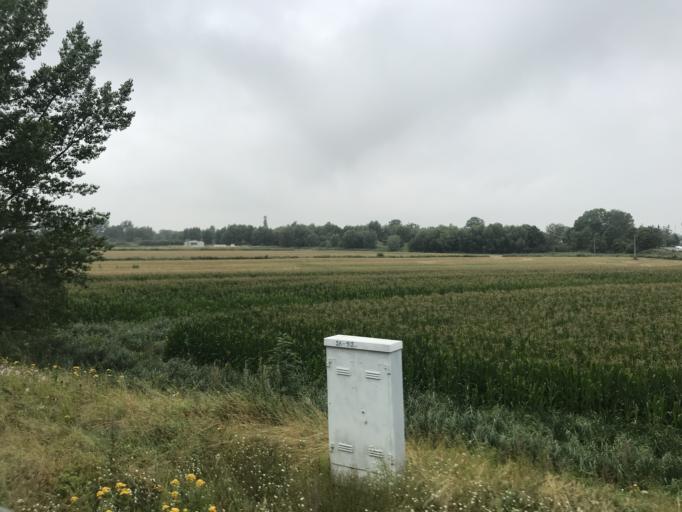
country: PL
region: Warmian-Masurian Voivodeship
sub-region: Powiat elblaski
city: Elblag
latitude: 54.1418
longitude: 19.3885
